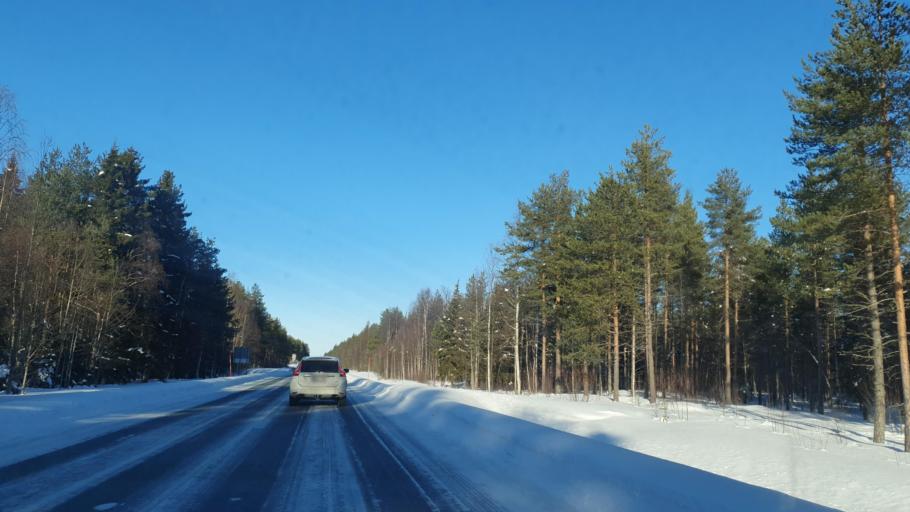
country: FI
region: Lapland
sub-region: Torniolaakso
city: Pello
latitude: 66.5952
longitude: 23.8876
